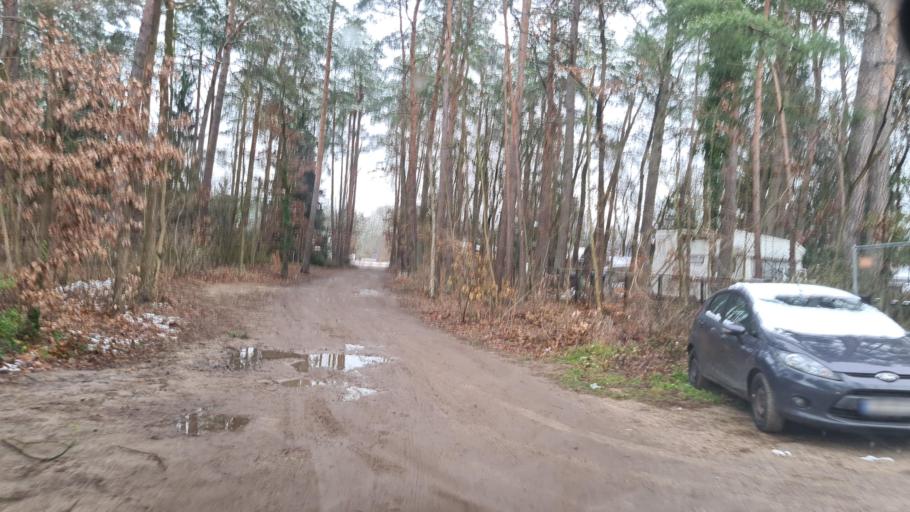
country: DE
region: Brandenburg
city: Grunheide
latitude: 52.4502
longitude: 13.8710
